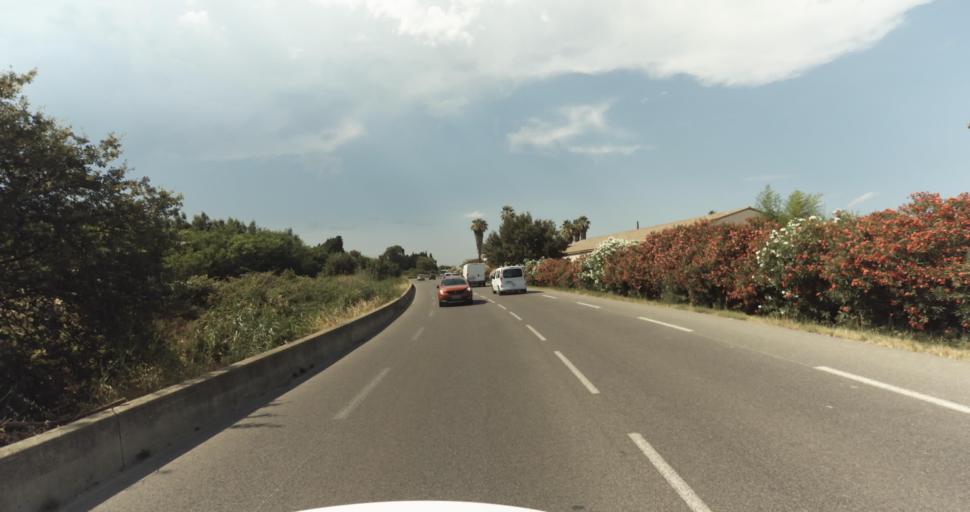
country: FR
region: Languedoc-Roussillon
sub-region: Departement des Pyrenees-Orientales
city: Alenya
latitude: 42.6366
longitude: 2.9752
